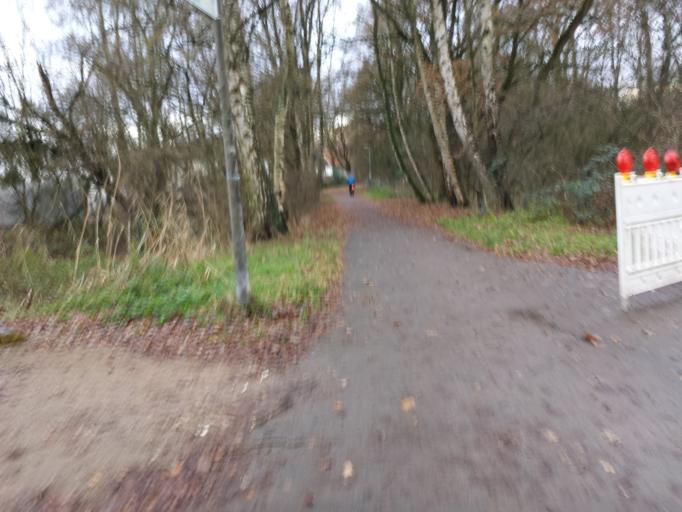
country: DE
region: Bremen
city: Bremen
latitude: 53.0981
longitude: 8.8609
